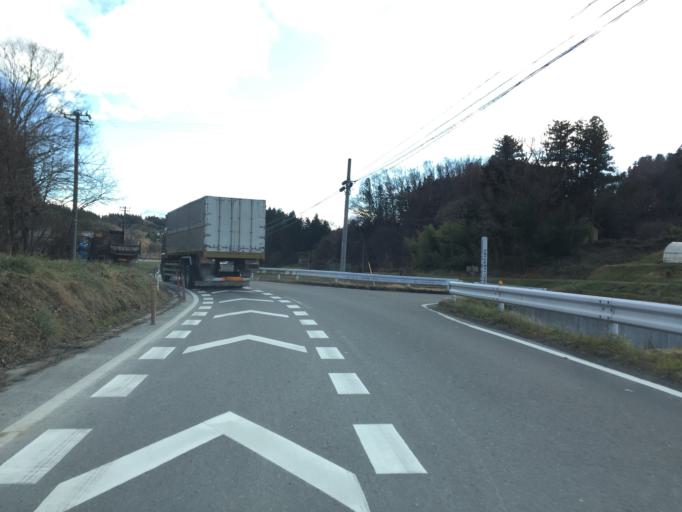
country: JP
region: Fukushima
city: Funehikimachi-funehiki
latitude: 37.5082
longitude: 140.5774
